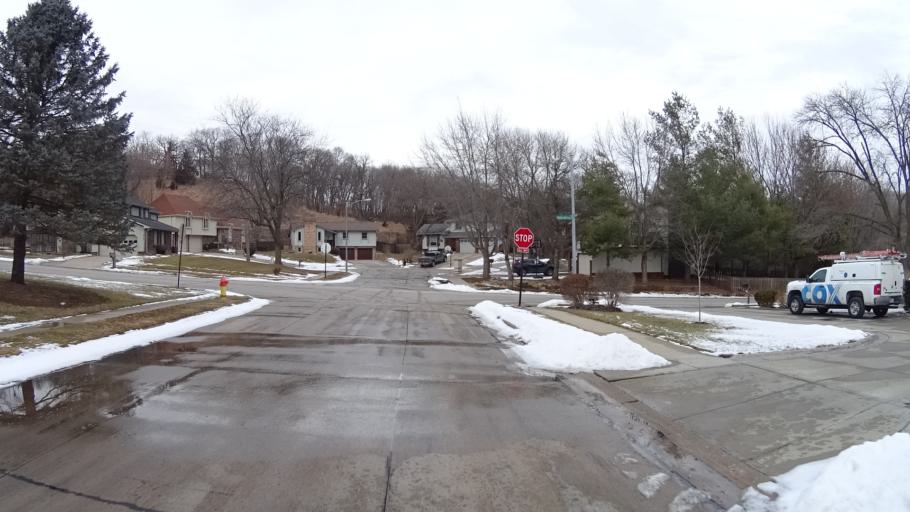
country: US
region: Nebraska
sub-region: Sarpy County
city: Bellevue
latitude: 41.1749
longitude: -95.9154
